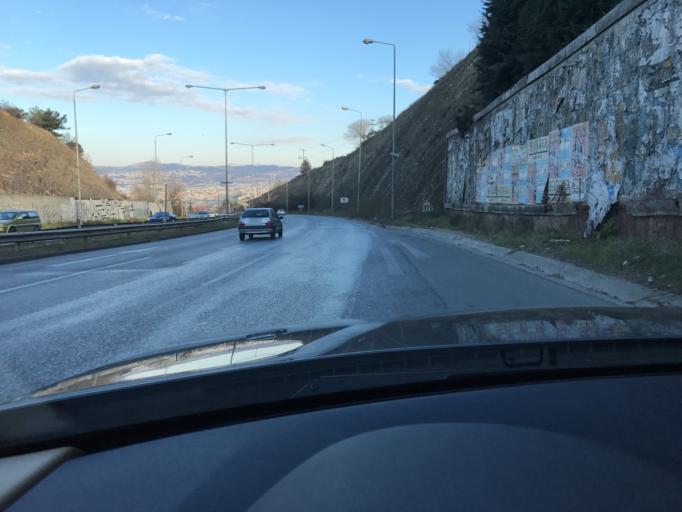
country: GR
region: Central Macedonia
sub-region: Nomos Thessalonikis
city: Polichni
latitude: 40.6611
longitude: 22.9685
